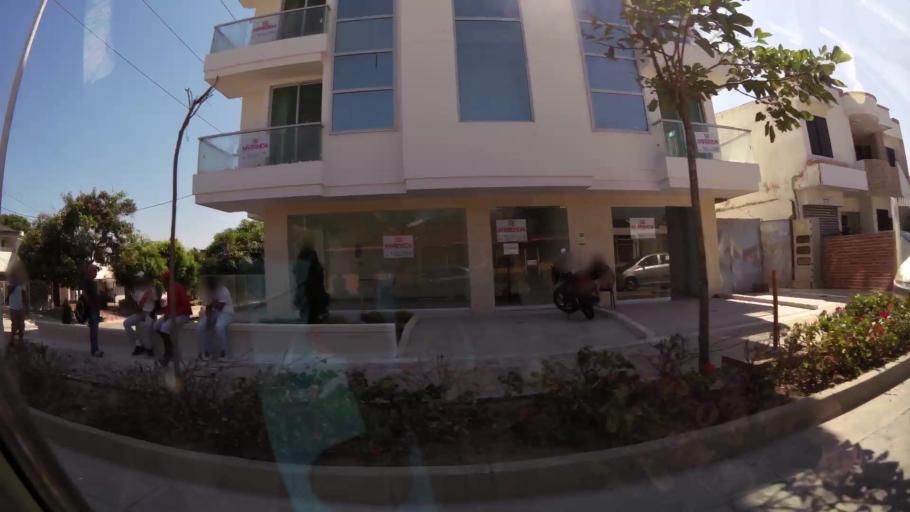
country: CO
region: Atlantico
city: Barranquilla
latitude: 11.0162
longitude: -74.8085
